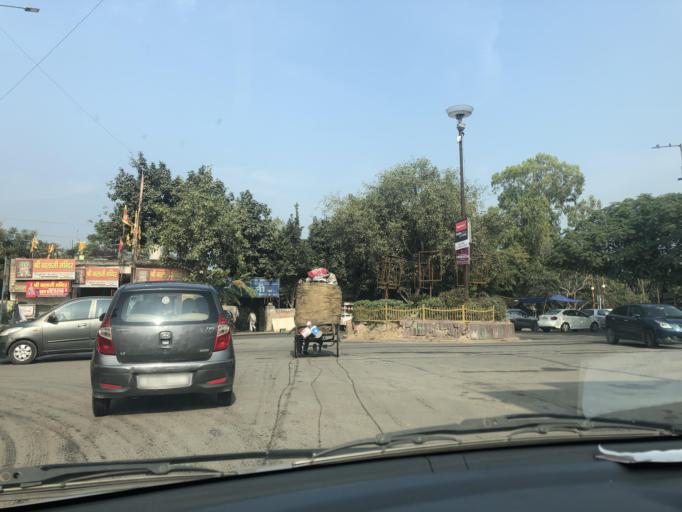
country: IN
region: Uttar Pradesh
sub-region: Gautam Buddha Nagar
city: Noida
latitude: 28.6481
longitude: 77.3596
